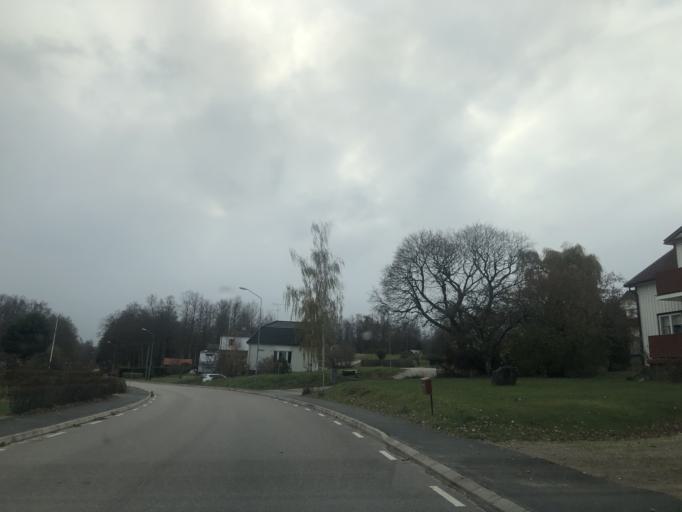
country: SE
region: Vaestra Goetaland
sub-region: Ulricehamns Kommun
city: Ulricehamn
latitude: 57.6747
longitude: 13.3708
